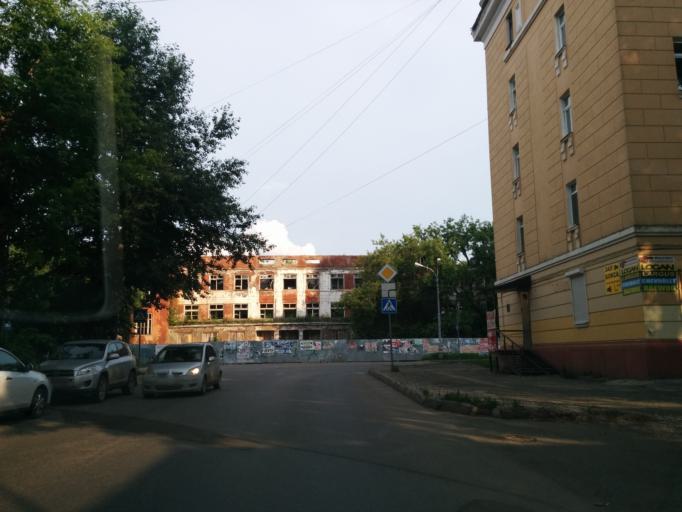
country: RU
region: Perm
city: Perm
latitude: 58.0263
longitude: 56.2962
